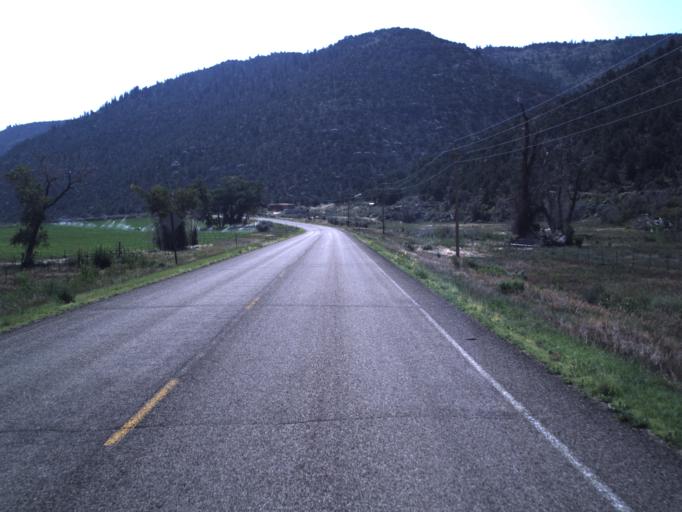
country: US
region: Utah
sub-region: Duchesne County
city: Duchesne
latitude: 40.2990
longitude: -110.6024
